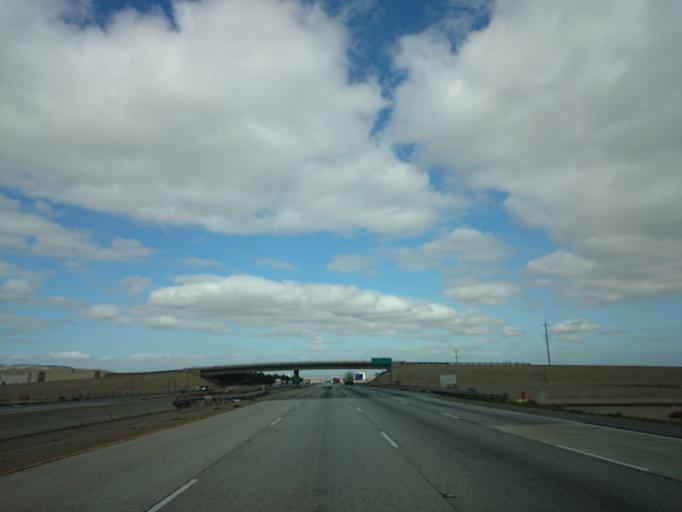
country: US
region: California
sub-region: Kern County
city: Frazier Park
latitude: 34.9707
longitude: -118.9402
